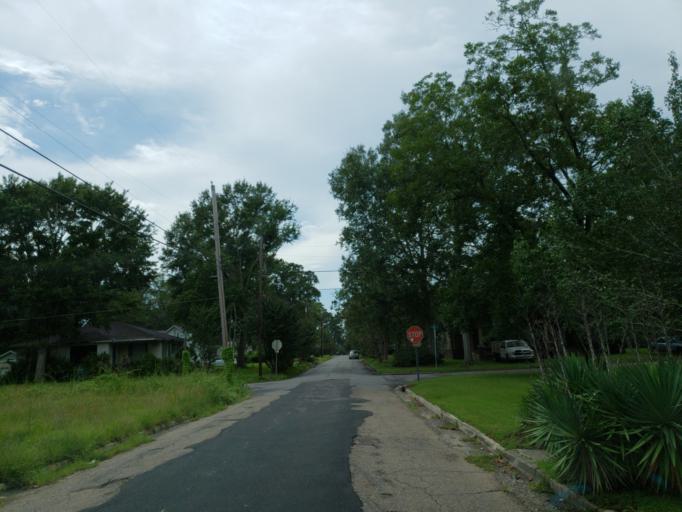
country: US
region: Mississippi
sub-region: Forrest County
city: Hattiesburg
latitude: 31.3229
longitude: -89.3090
